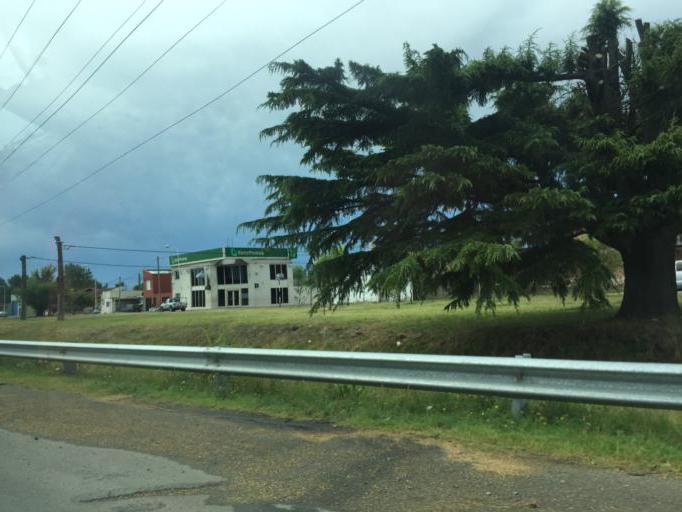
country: AR
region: Buenos Aires
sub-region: Partido de Tandil
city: Tandil
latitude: -37.3060
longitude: -59.1210
